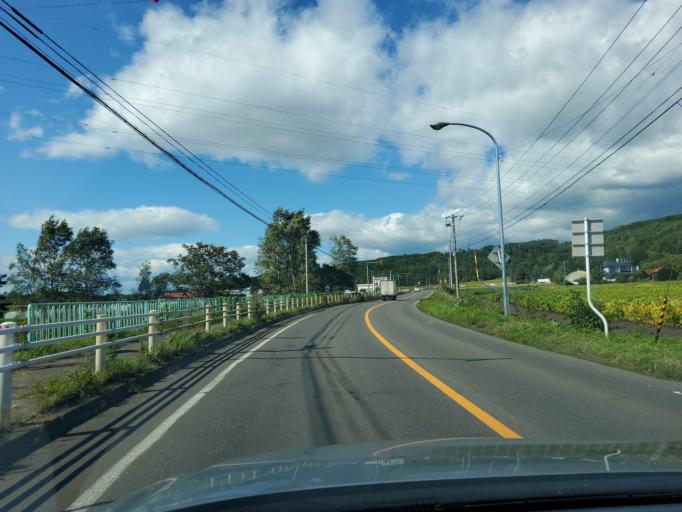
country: JP
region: Hokkaido
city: Obihiro
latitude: 42.9424
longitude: 143.2785
